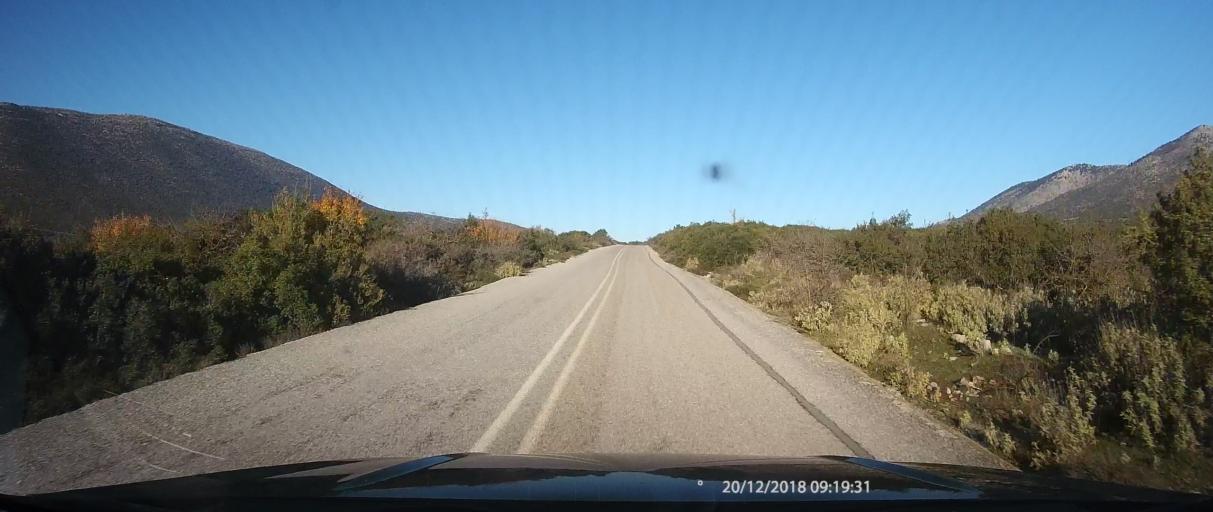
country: GR
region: Peloponnese
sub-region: Nomos Lakonias
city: Molaoi
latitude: 36.9196
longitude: 22.9387
